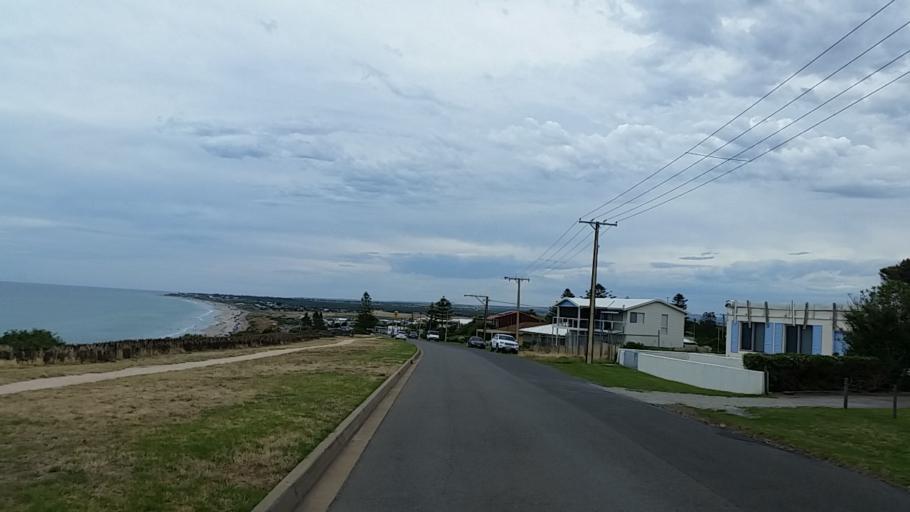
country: AU
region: South Australia
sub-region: Onkaparinga
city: Port Willunga
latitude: -35.3378
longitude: 138.4474
